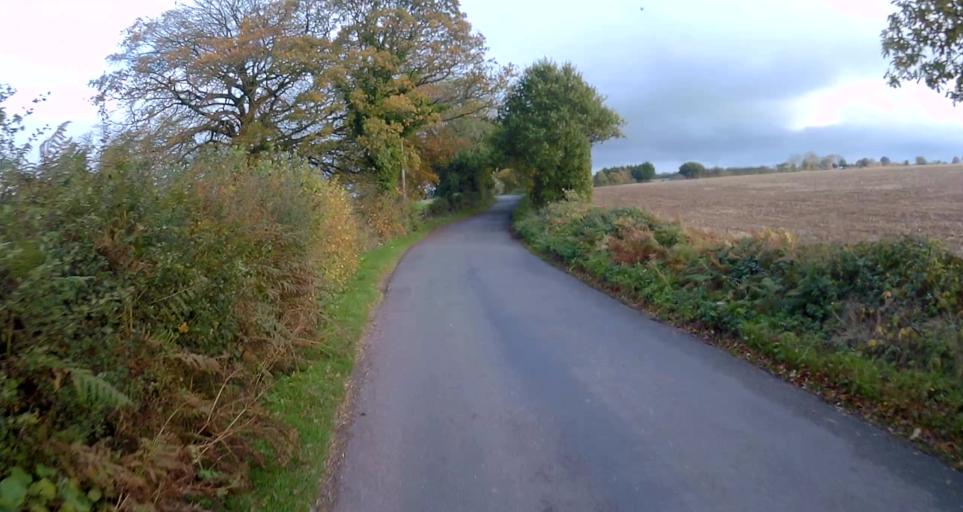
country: GB
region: England
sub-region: Hampshire
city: Four Marks
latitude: 51.1365
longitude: -1.1098
